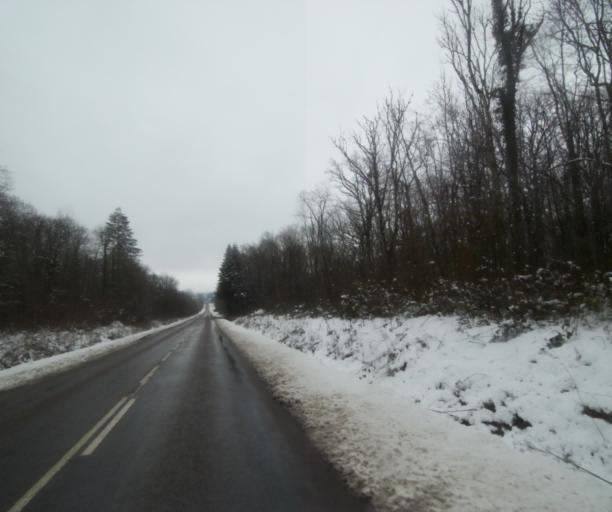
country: FR
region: Champagne-Ardenne
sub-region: Departement de la Haute-Marne
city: Wassy
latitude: 48.4954
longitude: 4.9233
